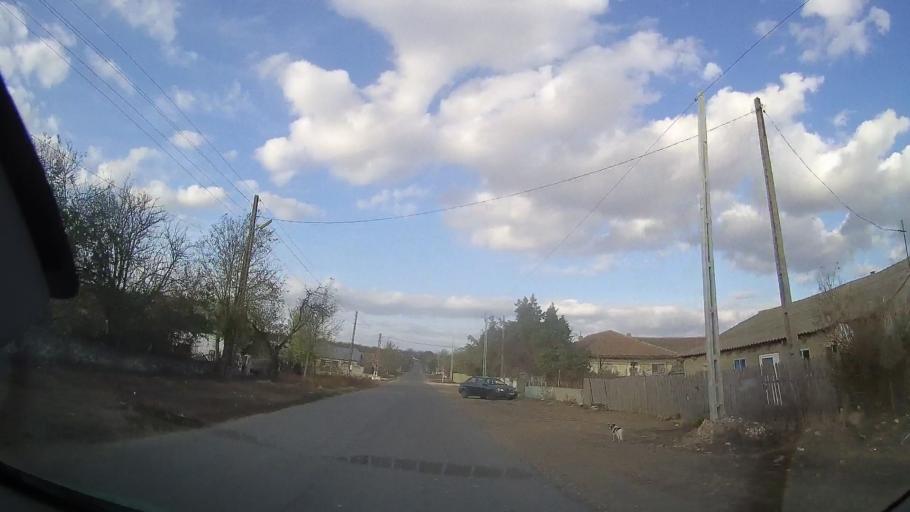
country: RO
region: Constanta
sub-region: Comuna Cerchezu
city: Cerchezu
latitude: 43.8559
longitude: 28.1012
